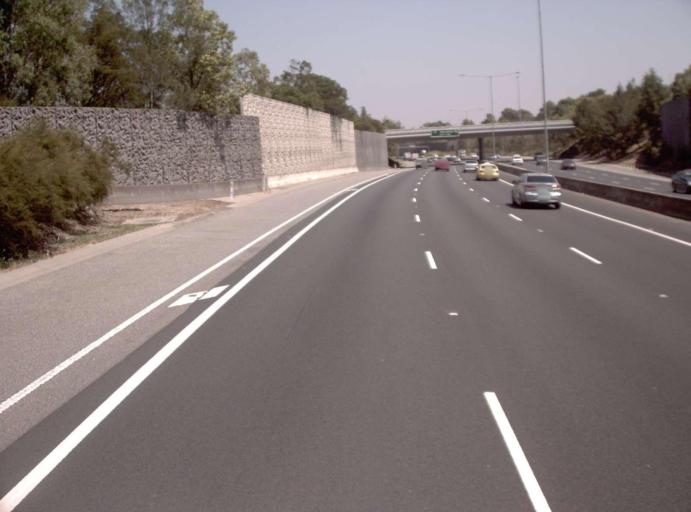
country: AU
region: Victoria
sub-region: Whitehorse
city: Box Hill North
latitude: -37.7970
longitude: 145.1207
